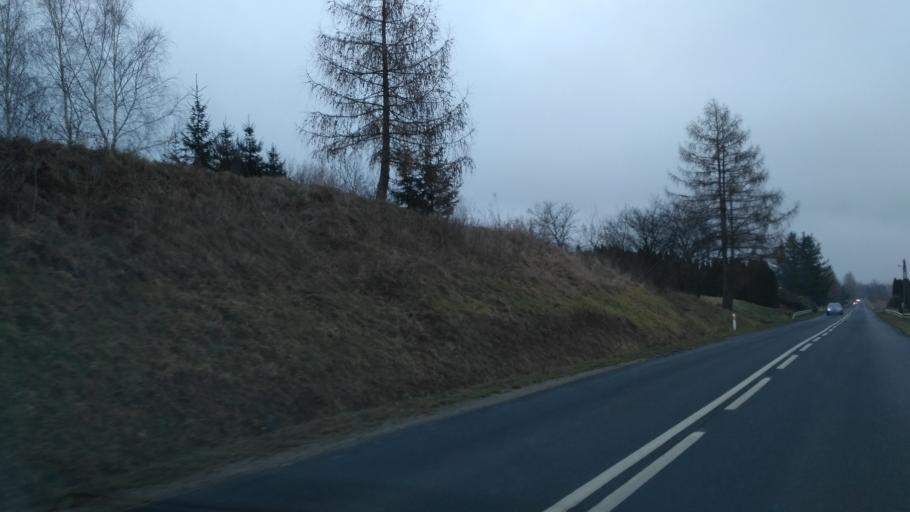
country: PL
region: Subcarpathian Voivodeship
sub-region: Powiat jaroslawski
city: Pruchnik
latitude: 49.9072
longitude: 22.5337
